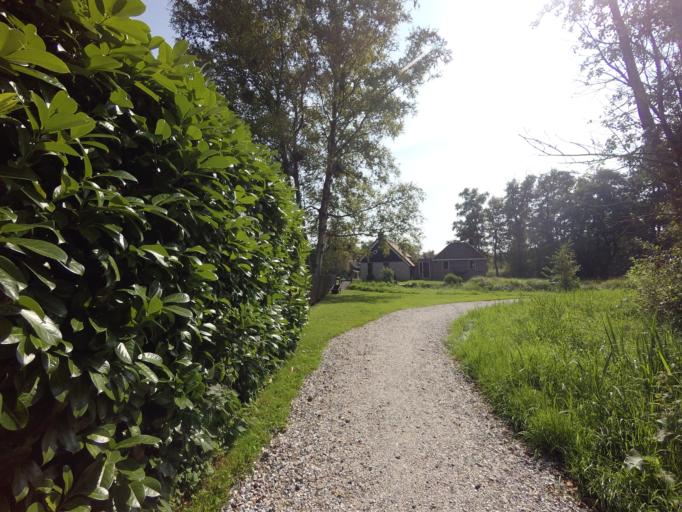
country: NL
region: Overijssel
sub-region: Gemeente Steenwijkerland
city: Oldemarkt
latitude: 52.8519
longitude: 5.9025
